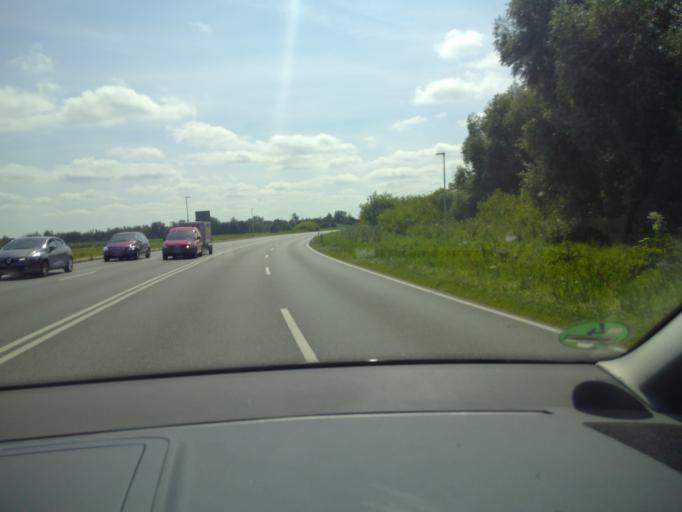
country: DE
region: Lower Saxony
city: Cuxhaven
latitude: 53.8334
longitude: 8.6813
